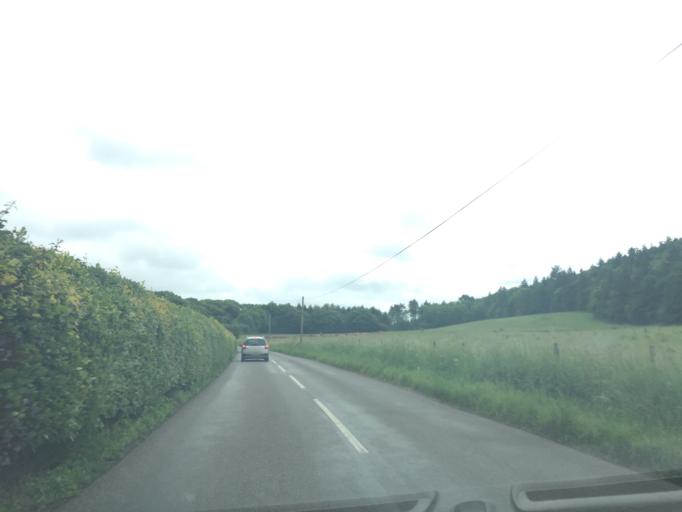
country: GB
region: England
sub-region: Dorset
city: Swanage
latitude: 50.6394
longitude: -2.0145
